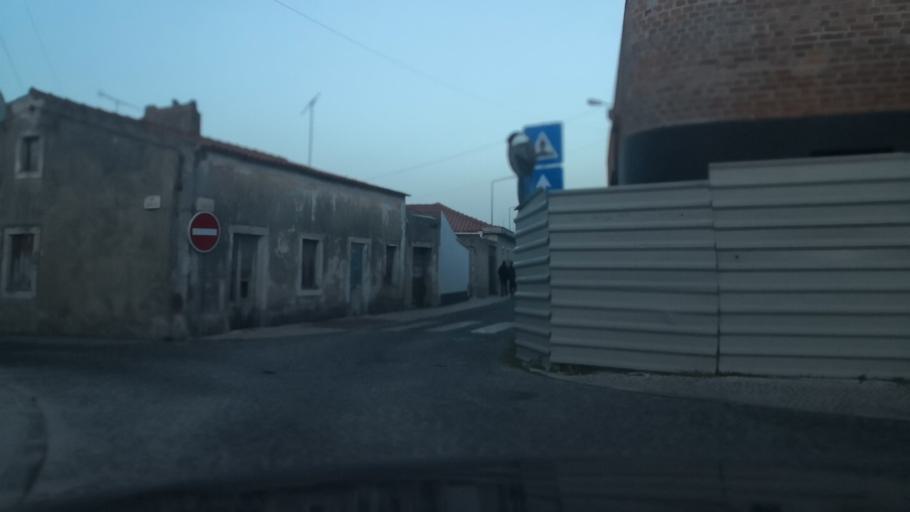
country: PT
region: Leiria
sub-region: Marinha Grande
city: Marinha Grande
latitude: 39.7515
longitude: -8.9318
